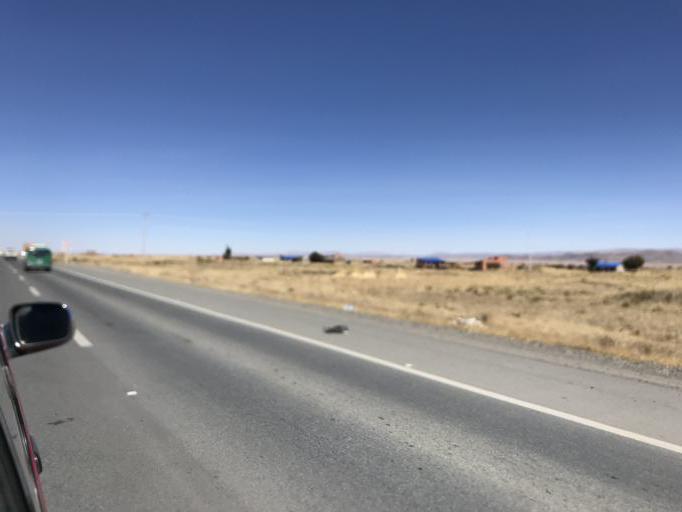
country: BO
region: La Paz
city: Batallas
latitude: -16.3511
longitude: -68.4024
